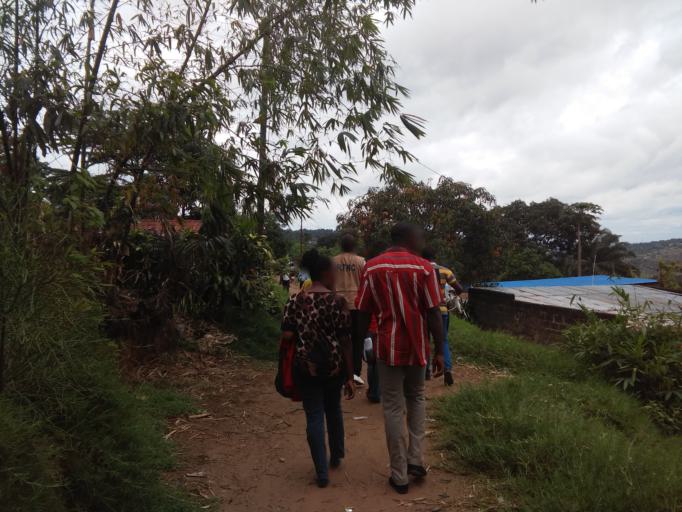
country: CD
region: Kinshasa
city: Masina
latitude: -4.4237
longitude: 15.3307
